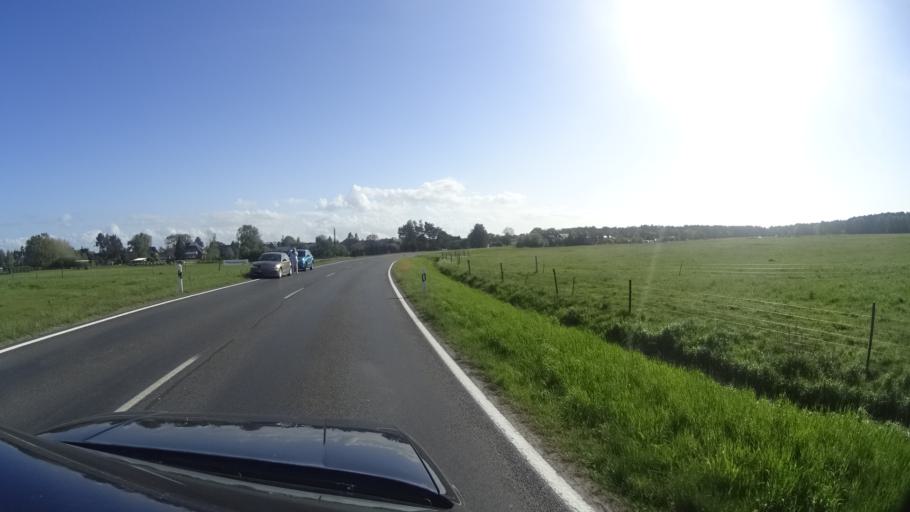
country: DE
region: Mecklenburg-Vorpommern
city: Ostseebad Prerow
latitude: 54.4135
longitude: 12.5788
